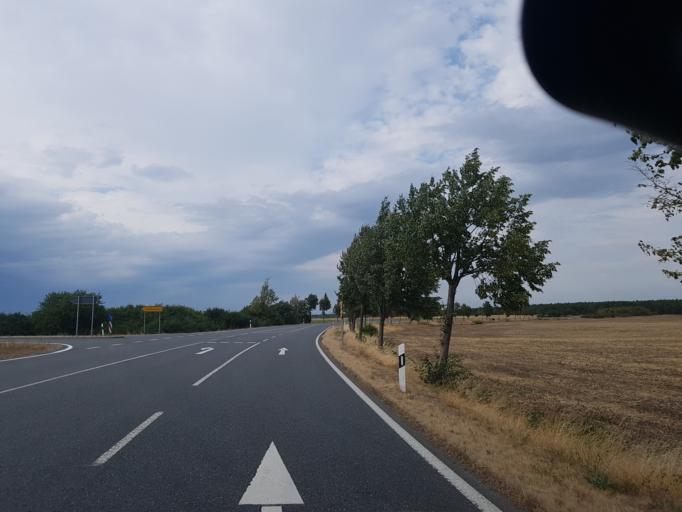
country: DE
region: Saxony
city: Strehla
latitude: 51.3597
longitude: 13.2617
